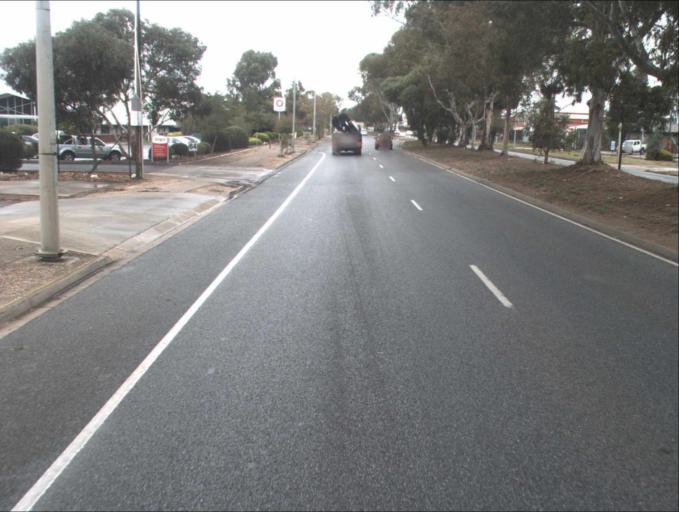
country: AU
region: South Australia
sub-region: Port Adelaide Enfield
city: Enfield
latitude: -34.8427
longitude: 138.5897
